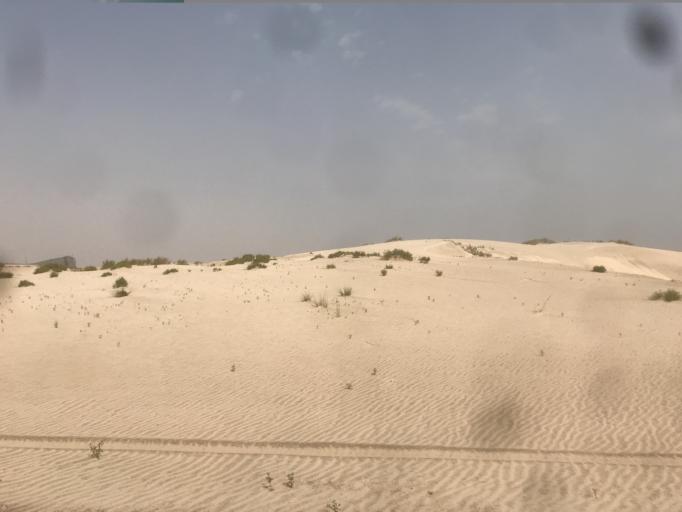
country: SA
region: Eastern Province
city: Abqaiq
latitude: 25.9069
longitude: 50.0000
